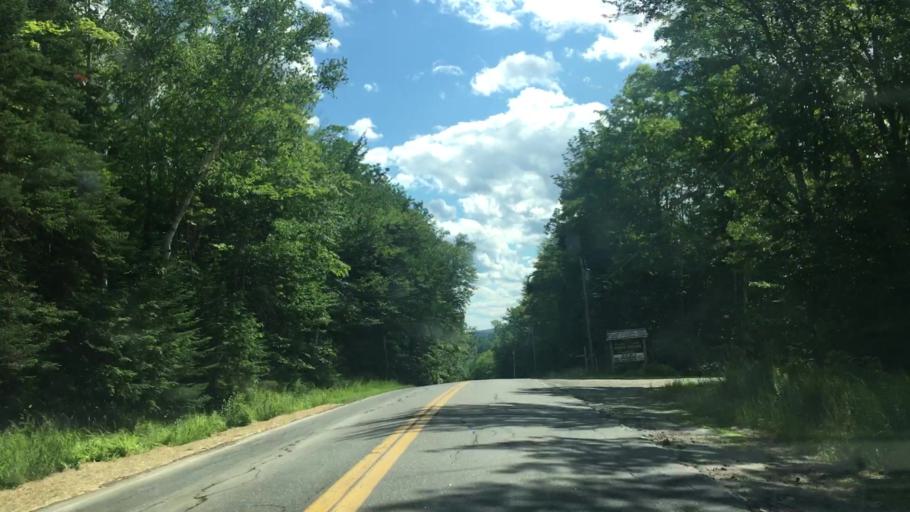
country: US
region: Maine
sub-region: Franklin County
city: Farmington
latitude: 44.6905
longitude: -70.1208
